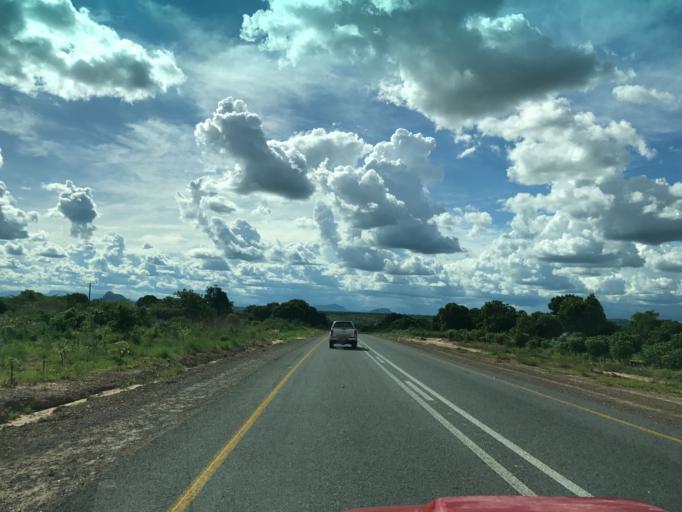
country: MZ
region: Nampula
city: Nampula
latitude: -15.0054
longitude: 39.0079
